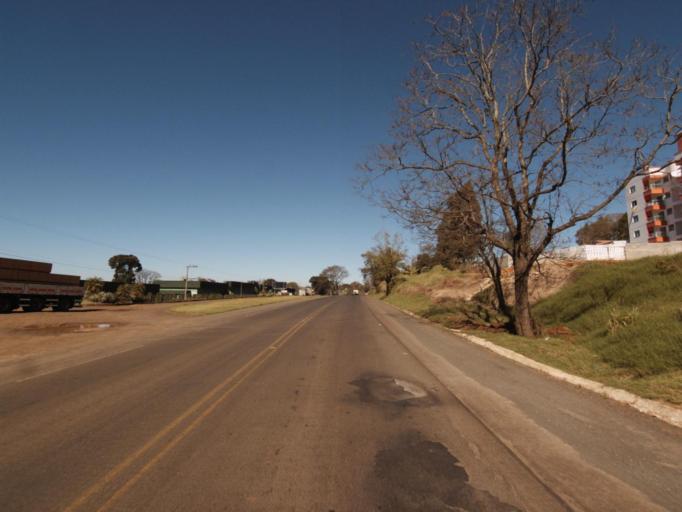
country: BR
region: Santa Catarina
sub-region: Chapeco
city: Chapeco
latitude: -26.8478
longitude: -52.9804
